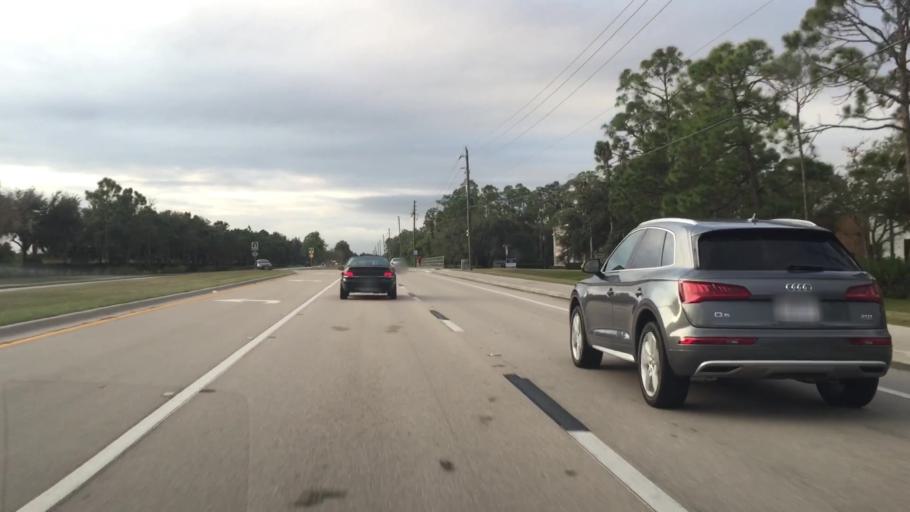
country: US
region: Florida
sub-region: Lee County
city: Gateway
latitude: 26.5635
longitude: -81.7867
